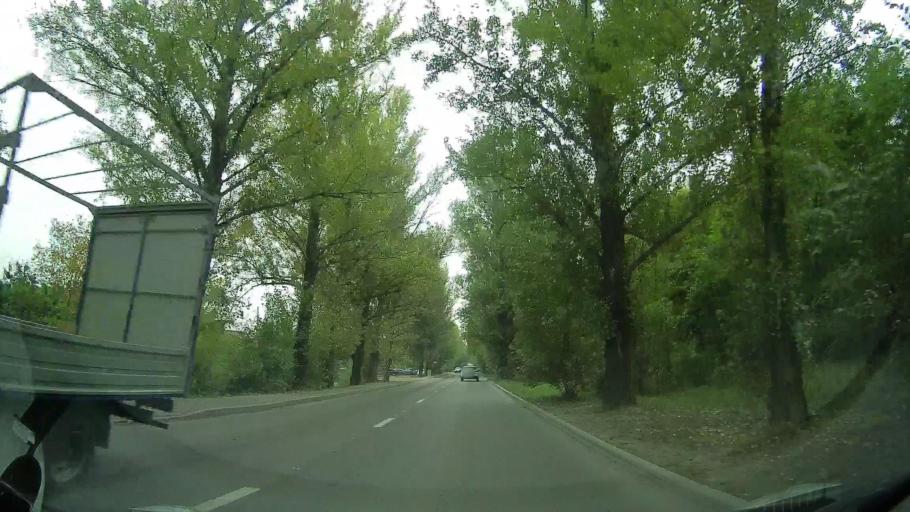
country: RU
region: Rostov
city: Severnyy
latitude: 47.2907
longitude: 39.6610
